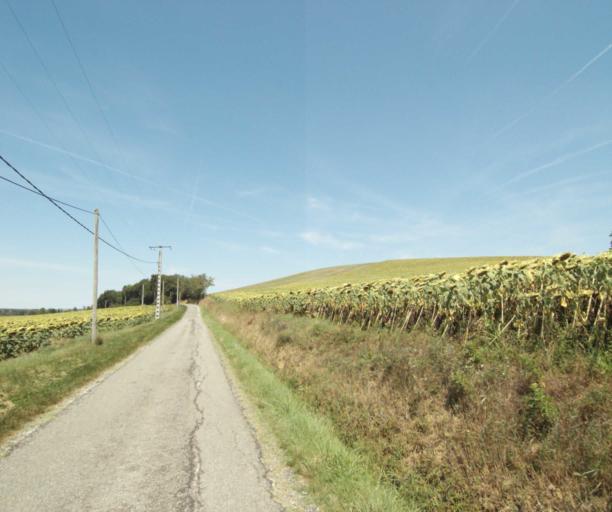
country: FR
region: Midi-Pyrenees
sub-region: Departement de l'Ariege
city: Lezat-sur-Leze
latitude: 43.2914
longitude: 1.3549
